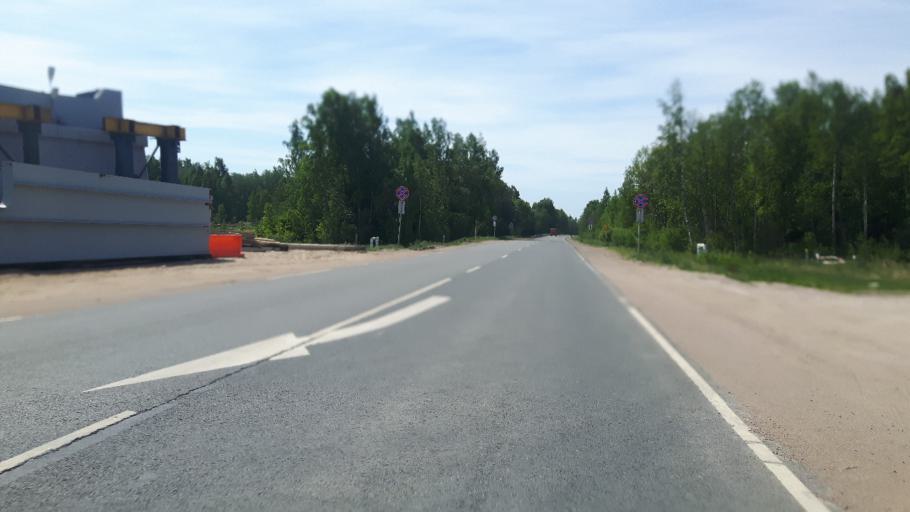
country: RU
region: Leningrad
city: Vistino
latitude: 59.6828
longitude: 28.4579
